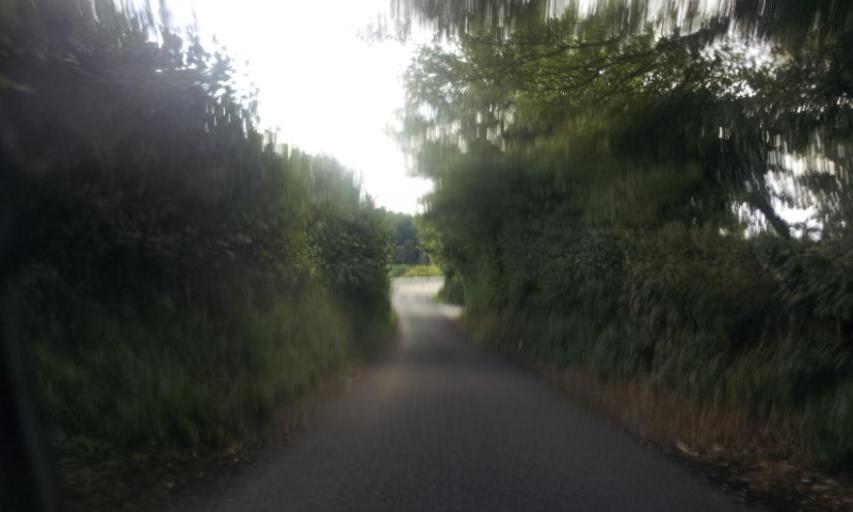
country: GB
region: England
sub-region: Kent
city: Newington
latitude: 51.3372
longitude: 0.6692
